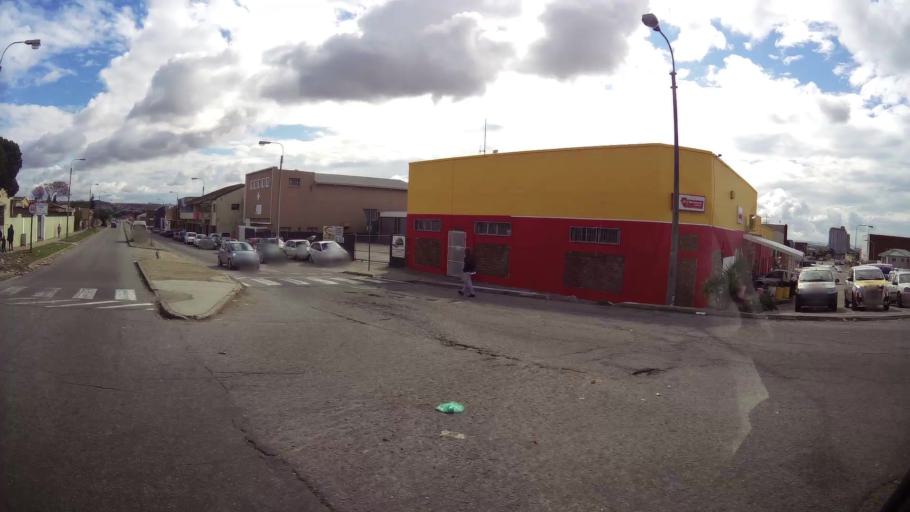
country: ZA
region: Eastern Cape
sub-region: Nelson Mandela Bay Metropolitan Municipality
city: Port Elizabeth
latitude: -33.9291
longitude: 25.5693
